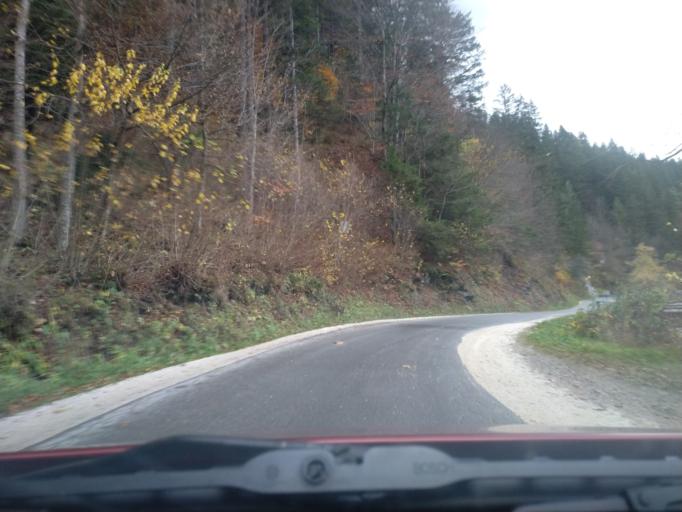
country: SI
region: Luce
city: Luce
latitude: 46.3353
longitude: 14.7251
